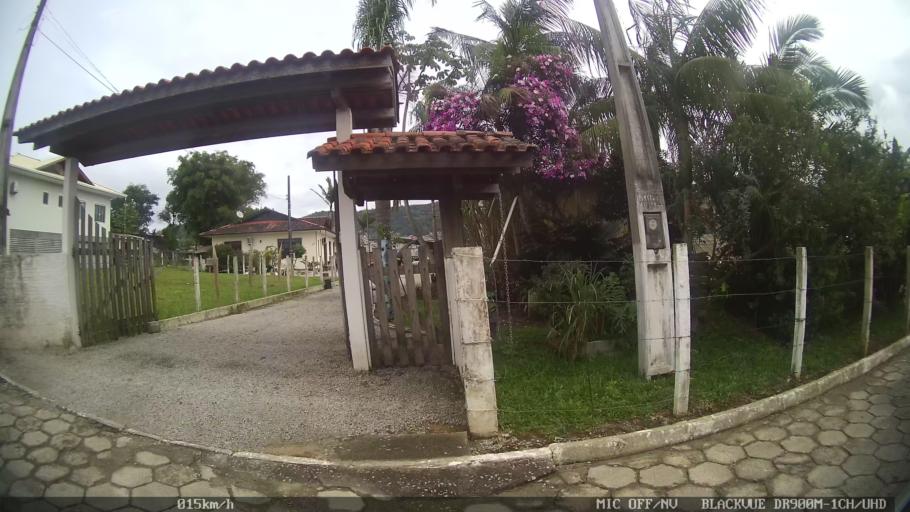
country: BR
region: Santa Catarina
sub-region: Biguacu
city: Biguacu
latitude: -27.5384
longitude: -48.6387
